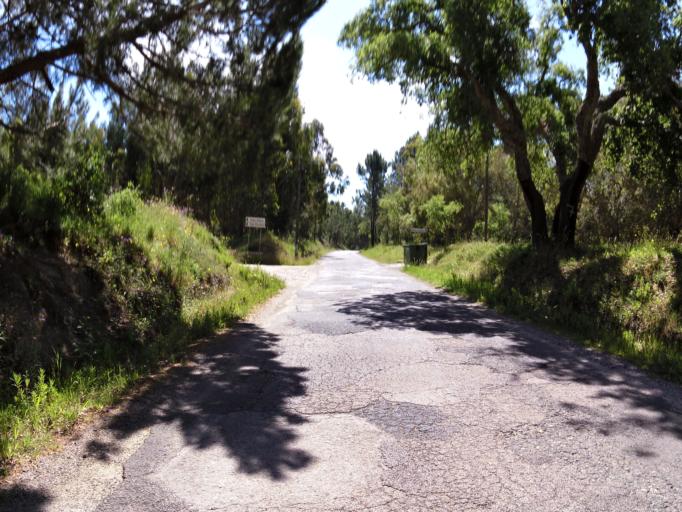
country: PT
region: Setubal
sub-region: Sines
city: Porto Covo
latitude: 37.9360
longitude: -8.7640
